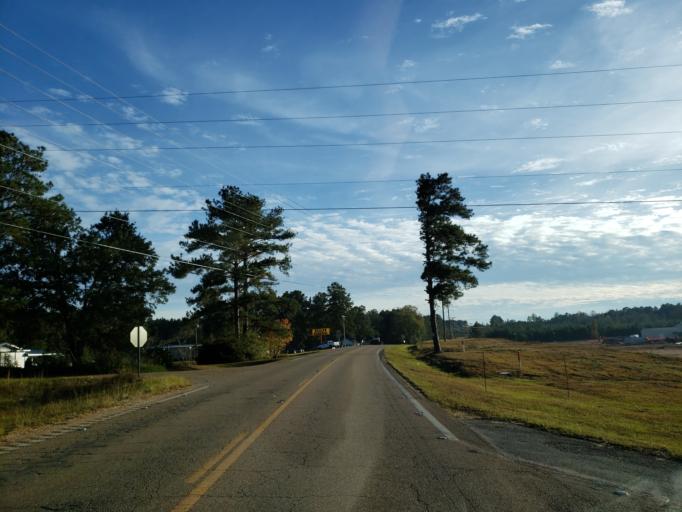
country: US
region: Mississippi
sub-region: Lamar County
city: West Hattiesburg
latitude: 31.2992
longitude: -89.4691
